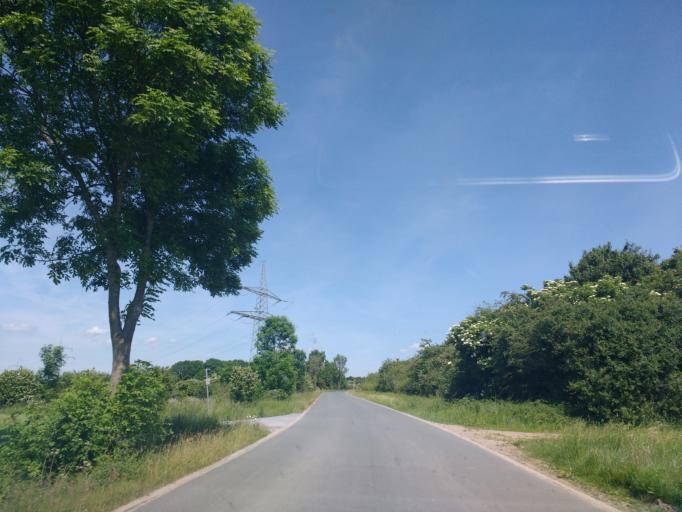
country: DE
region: North Rhine-Westphalia
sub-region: Regierungsbezirk Detmold
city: Paderborn
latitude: 51.6907
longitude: 8.7174
